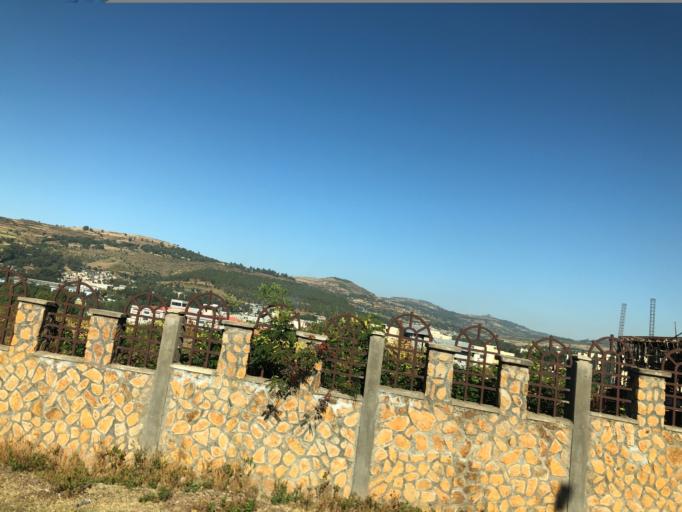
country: ET
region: Amhara
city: Gondar
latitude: 12.5738
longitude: 37.4454
